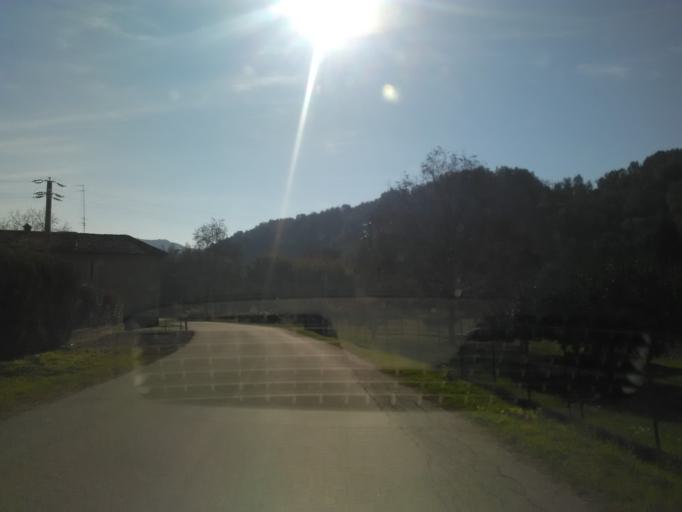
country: IT
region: Piedmont
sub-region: Provincia di Vercelli
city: Guardabosone
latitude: 45.7011
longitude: 8.2359
